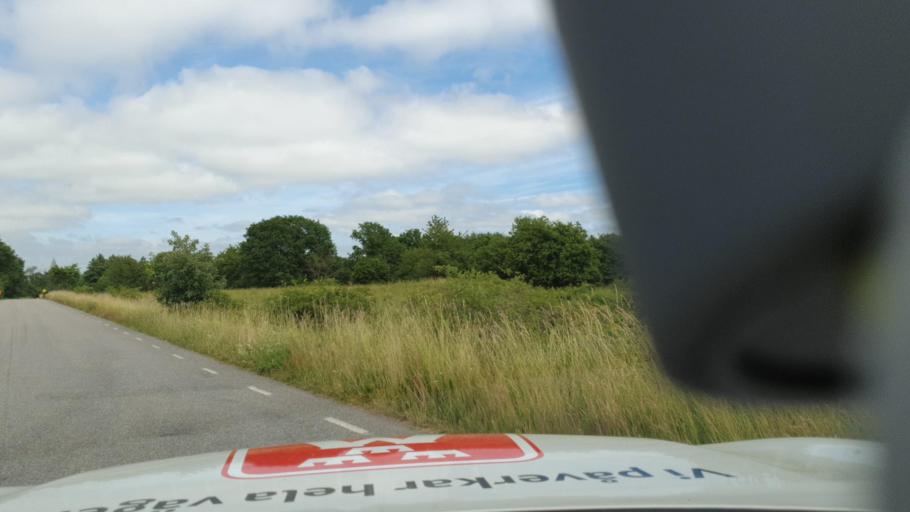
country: SE
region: Vaestra Goetaland
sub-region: Gotene Kommun
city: Kallby
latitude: 58.5353
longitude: 13.3972
